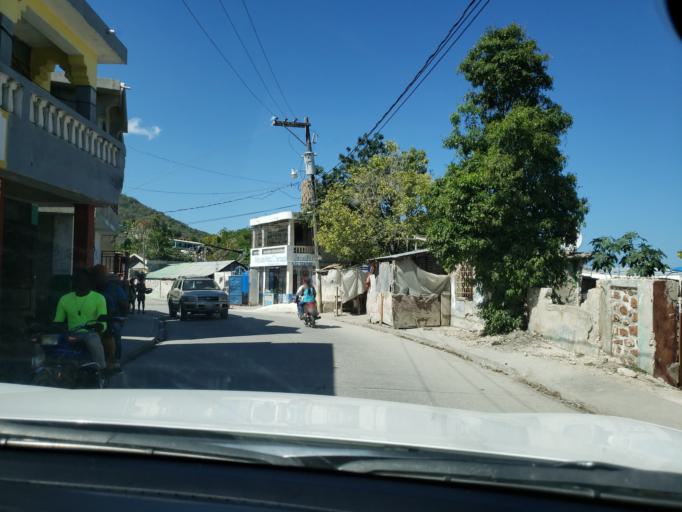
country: HT
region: Nippes
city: Miragoane
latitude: 18.4432
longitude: -73.0931
